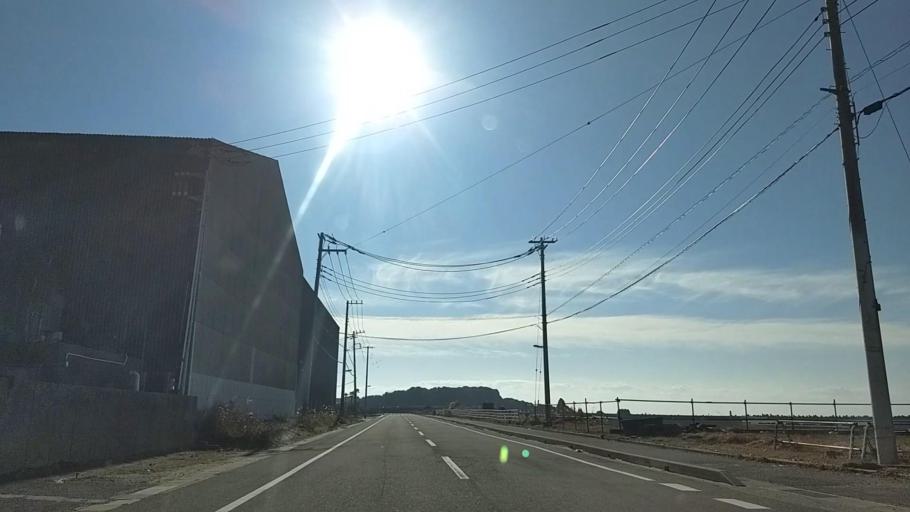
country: JP
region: Chiba
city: Hasaki
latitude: 35.7030
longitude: 140.8446
